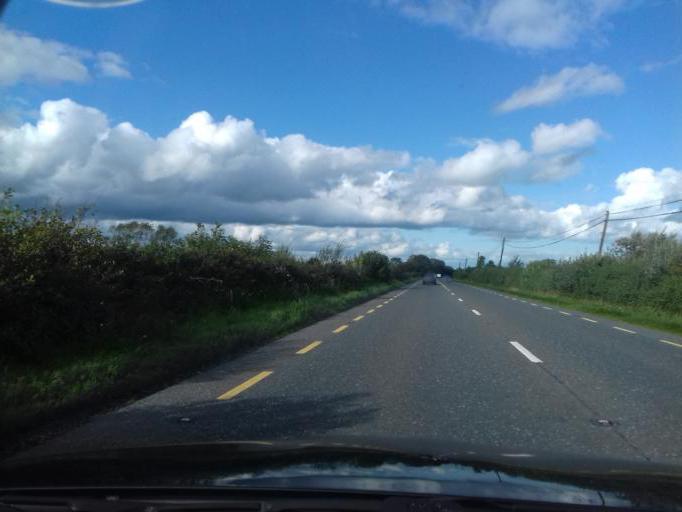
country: IE
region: Leinster
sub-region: An Iarmhi
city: Kilbeggan
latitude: 53.3361
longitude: -7.5094
